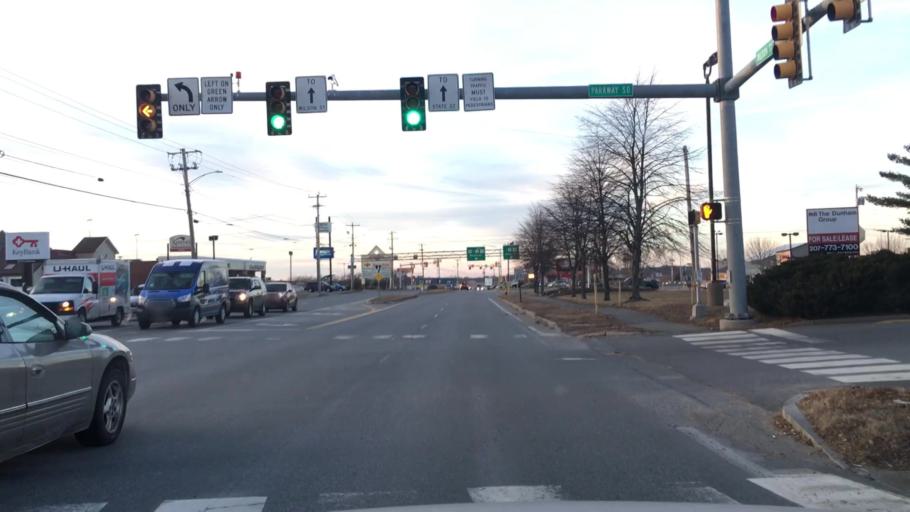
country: US
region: Maine
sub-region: Penobscot County
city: Brewer
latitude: 44.7837
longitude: -68.7503
